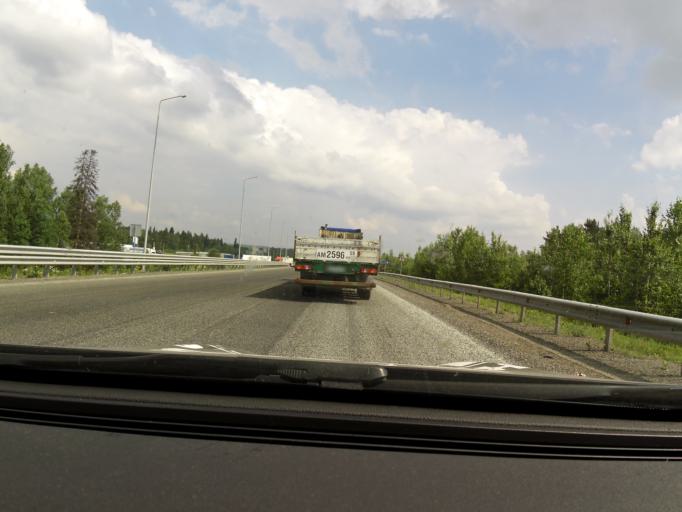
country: RU
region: Sverdlovsk
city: Ufimskiy
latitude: 56.7632
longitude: 58.1454
